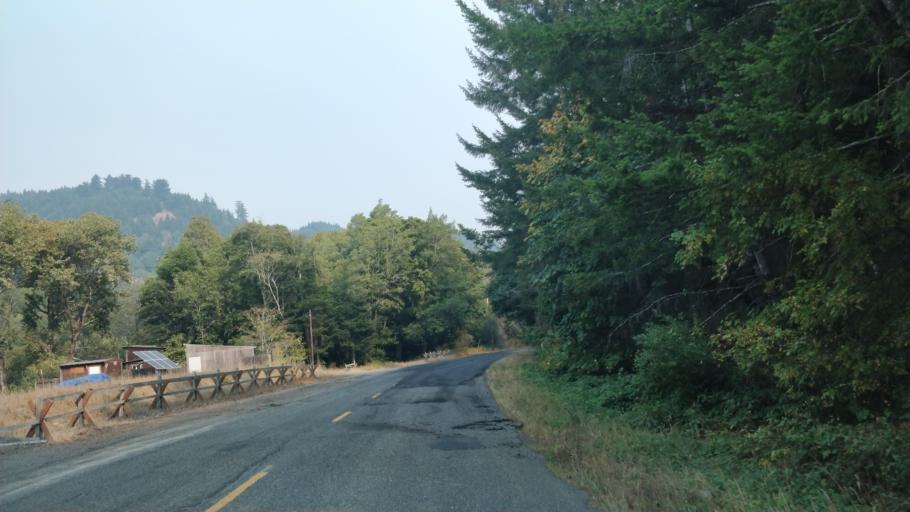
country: US
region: California
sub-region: Humboldt County
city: Rio Dell
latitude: 40.3109
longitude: -124.2653
